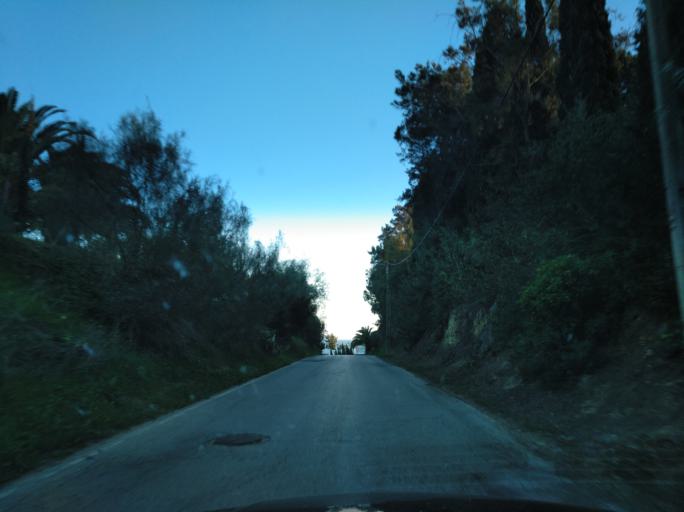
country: PT
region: Faro
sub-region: Tavira
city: Tavira
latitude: 37.1559
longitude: -7.5537
